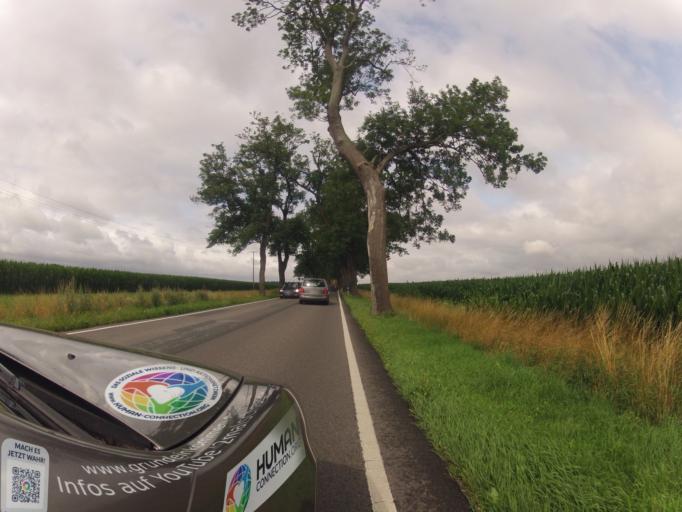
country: DE
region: Mecklenburg-Vorpommern
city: Anklam
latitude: 53.9041
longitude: 13.7589
